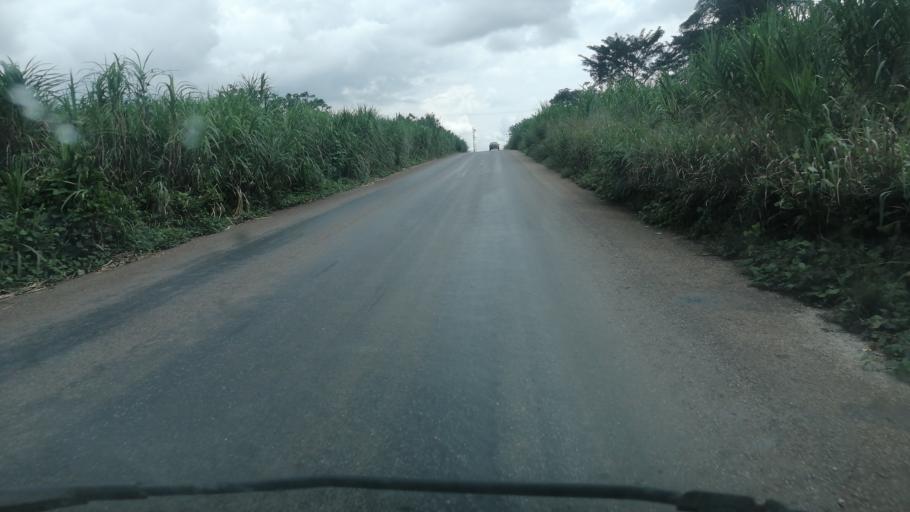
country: GH
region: Western
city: Bibiani
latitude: 6.8688
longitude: -2.4396
